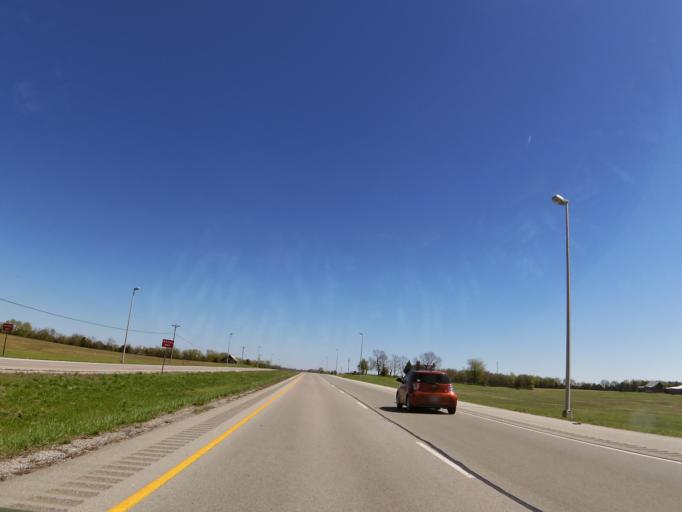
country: US
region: Kentucky
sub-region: Warren County
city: Bowling Green
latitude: 36.9398
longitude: -86.5316
